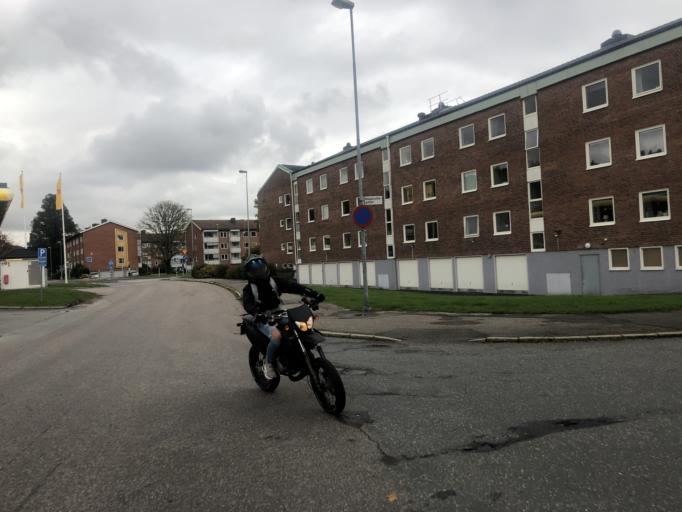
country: SE
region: Vaestra Goetaland
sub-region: Molndal
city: Moelndal
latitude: 57.6606
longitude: 11.9986
